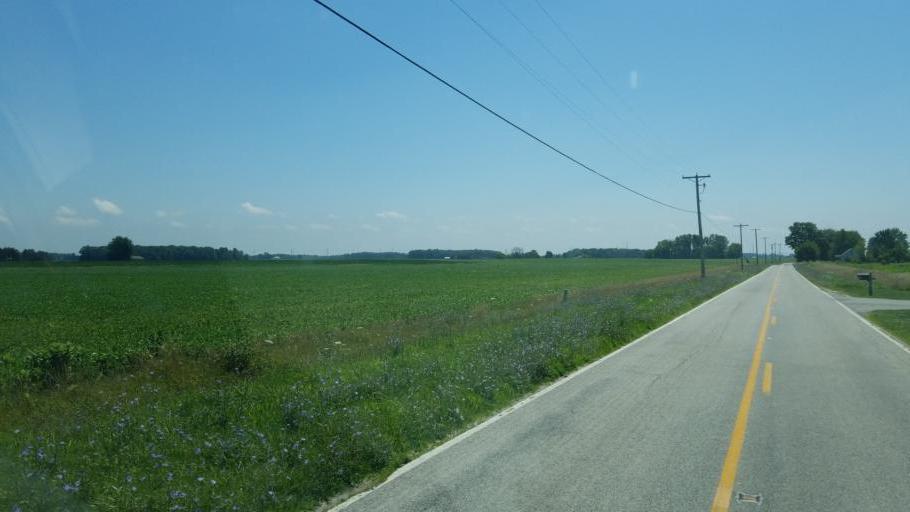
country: US
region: Ohio
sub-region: Sandusky County
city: Fremont
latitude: 41.4182
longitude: -83.0638
